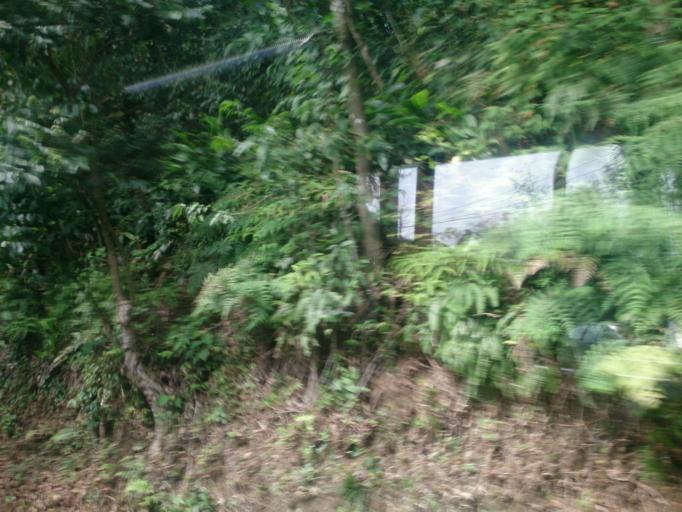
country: TW
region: Taipei
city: Taipei
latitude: 25.1607
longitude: 121.5454
